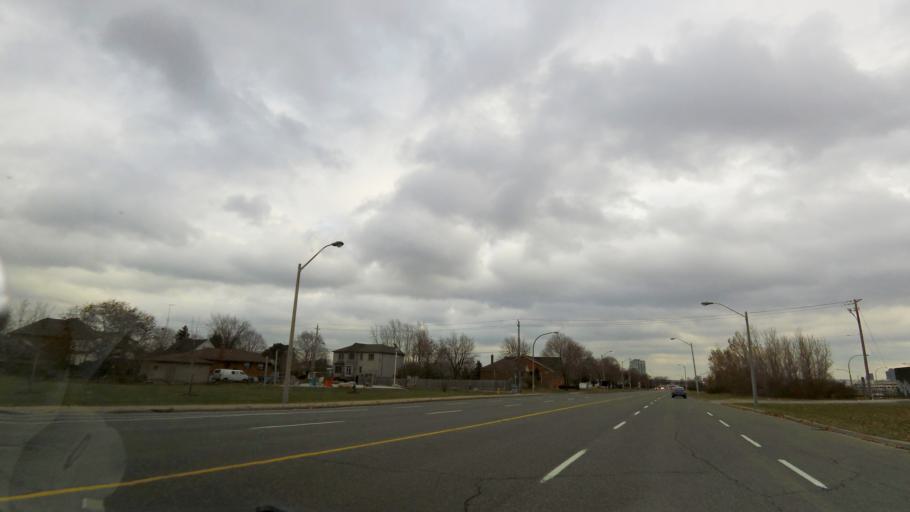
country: CA
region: Ontario
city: North York
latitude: 43.7413
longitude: -79.4519
